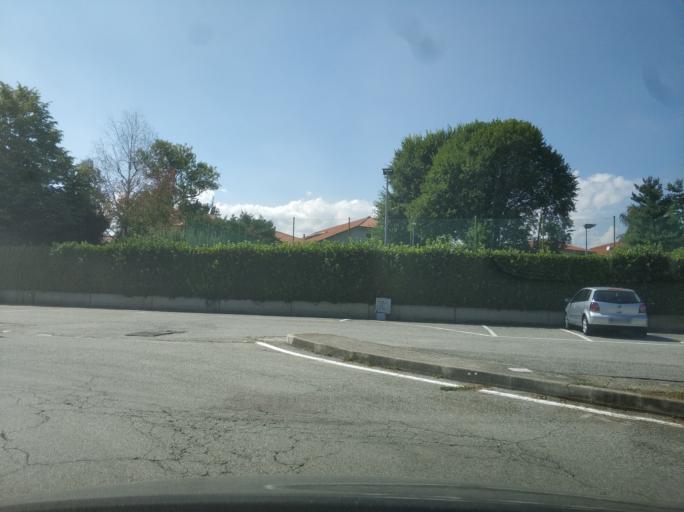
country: IT
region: Piedmont
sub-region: Provincia di Torino
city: Rivarolo Canavese
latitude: 45.3244
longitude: 7.7207
